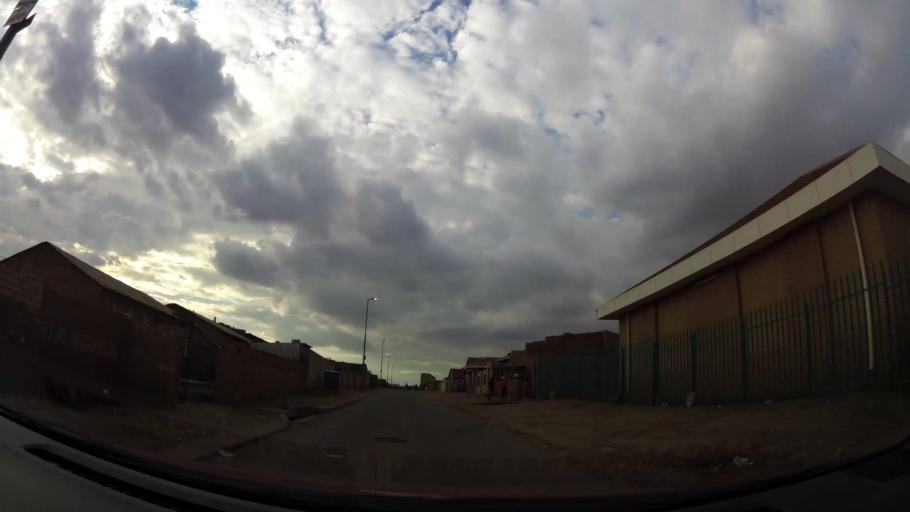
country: ZA
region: Gauteng
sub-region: City of Johannesburg Metropolitan Municipality
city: Soweto
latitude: -26.2449
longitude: 27.8153
